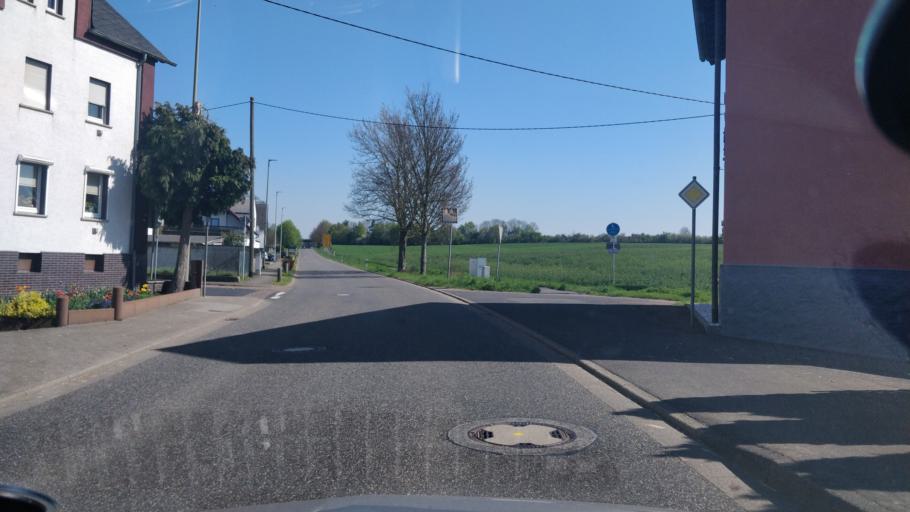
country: DE
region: Hesse
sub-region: Regierungsbezirk Giessen
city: Dehrn
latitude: 50.4492
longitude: 8.0816
